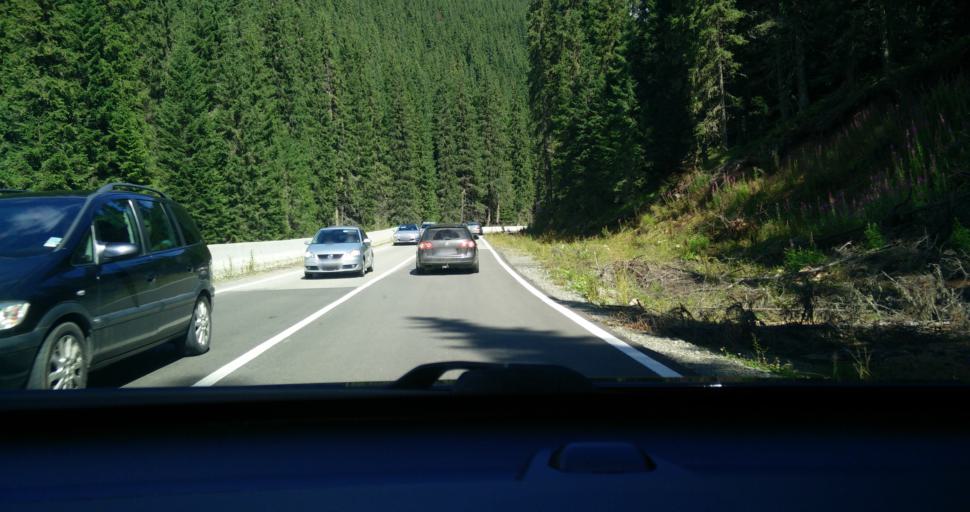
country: RO
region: Hunedoara
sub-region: Oras Petrila
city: Petrila
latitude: 45.5098
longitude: 23.6496
